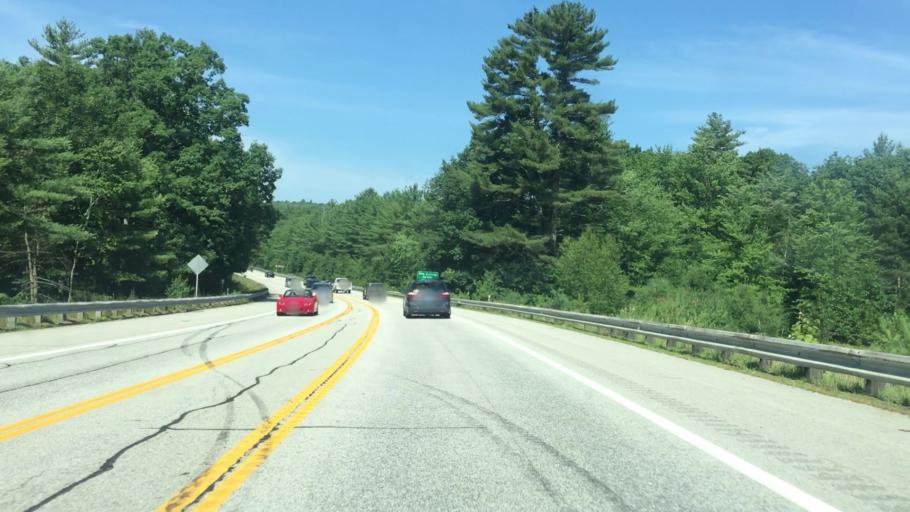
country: US
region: New Hampshire
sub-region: Merrimack County
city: Henniker
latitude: 43.1907
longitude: -71.8137
